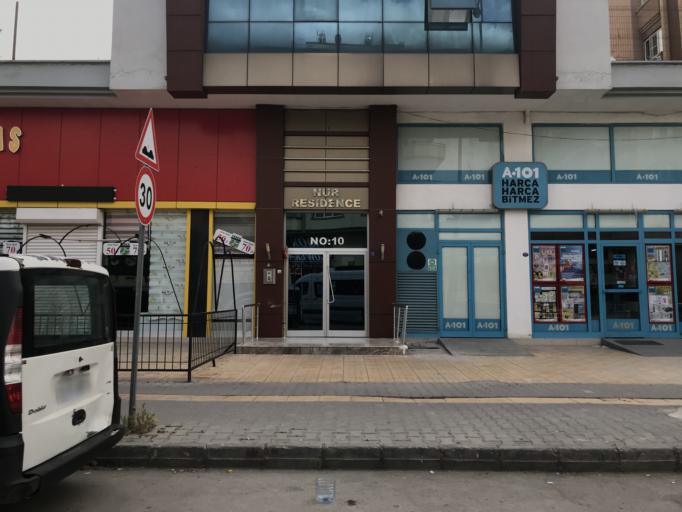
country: TR
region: Gaziantep
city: Sahinbey
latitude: 37.0532
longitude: 37.3346
